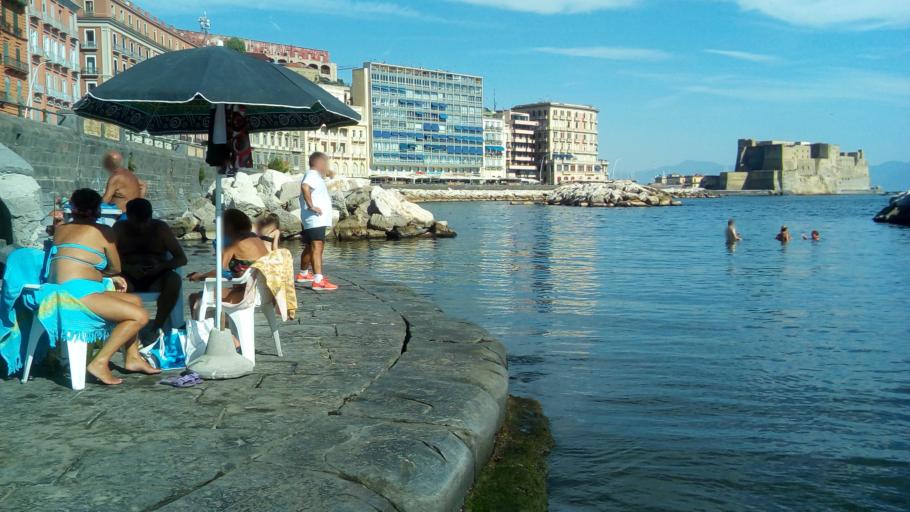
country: IT
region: Campania
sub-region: Provincia di Napoli
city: Napoli
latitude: 40.8314
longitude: 14.2410
